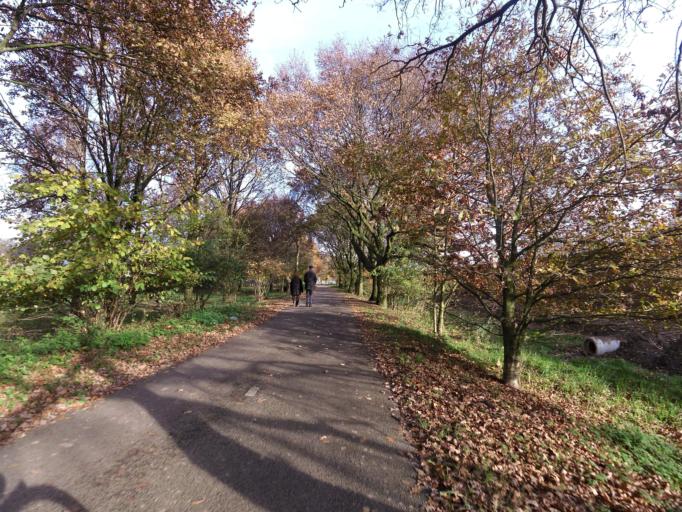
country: NL
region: Gelderland
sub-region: Gemeente Doetinchem
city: Doetinchem
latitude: 51.9614
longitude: 6.3108
